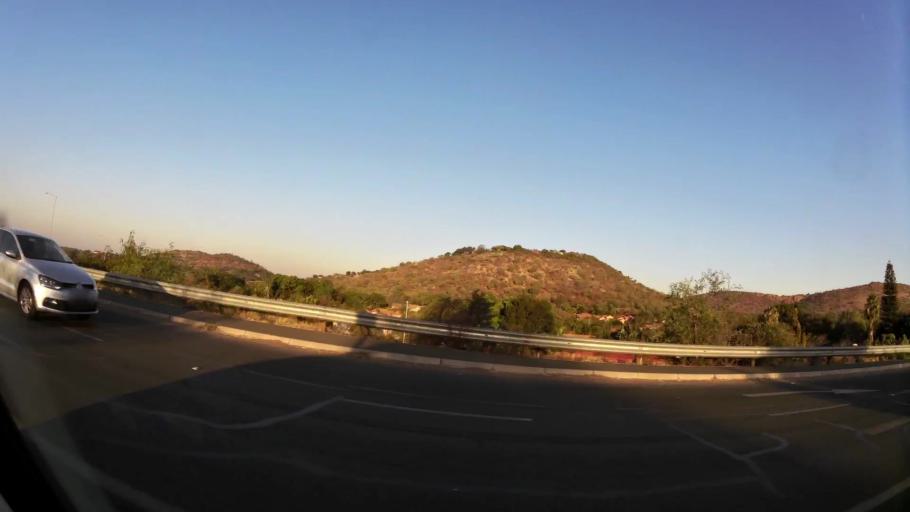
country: ZA
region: North-West
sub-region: Bojanala Platinum District Municipality
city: Rustenburg
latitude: -25.6907
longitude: 27.2259
